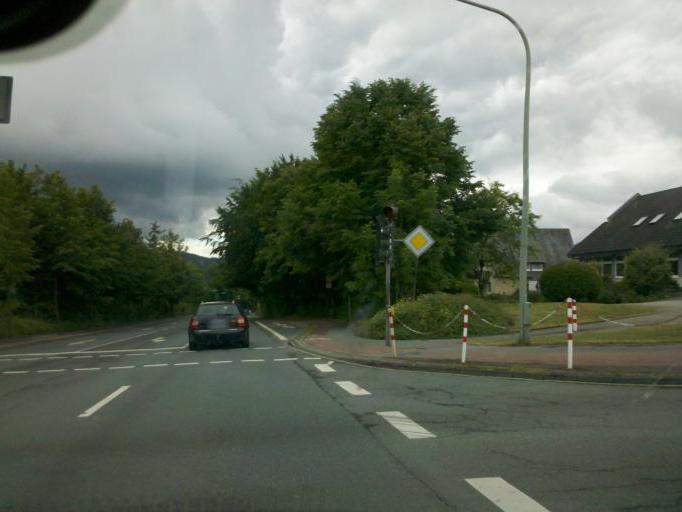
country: DE
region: North Rhine-Westphalia
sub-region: Regierungsbezirk Arnsberg
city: Meschede
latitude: 51.3600
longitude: 8.2867
